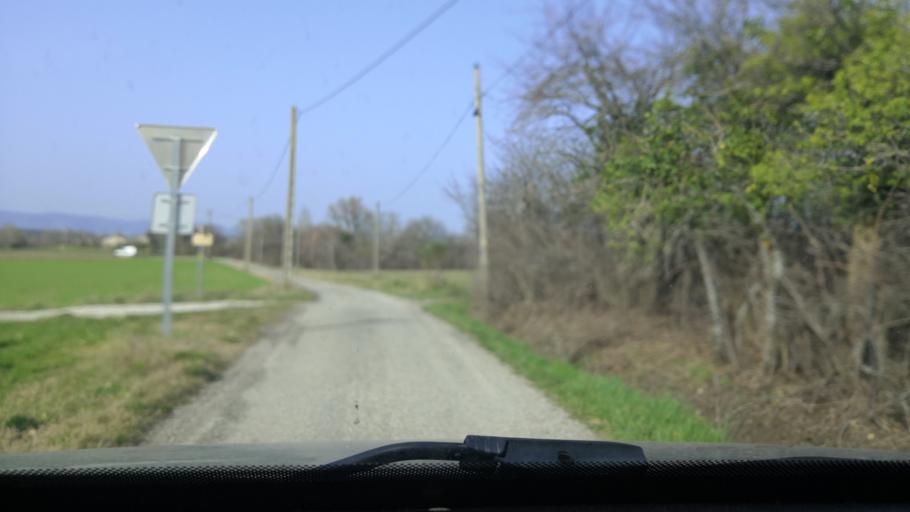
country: FR
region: Rhone-Alpes
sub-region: Departement de la Drome
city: La Begude-de-Mazenc
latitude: 44.5377
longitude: 4.9245
